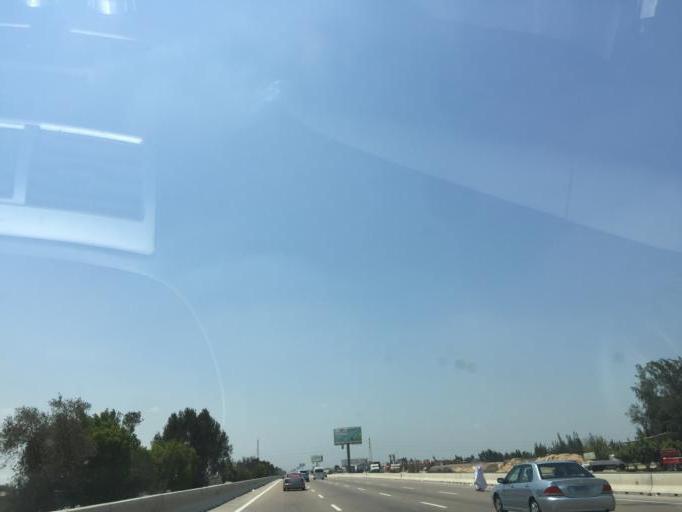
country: EG
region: Al Buhayrah
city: Beheira
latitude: 30.4135
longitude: 30.3559
